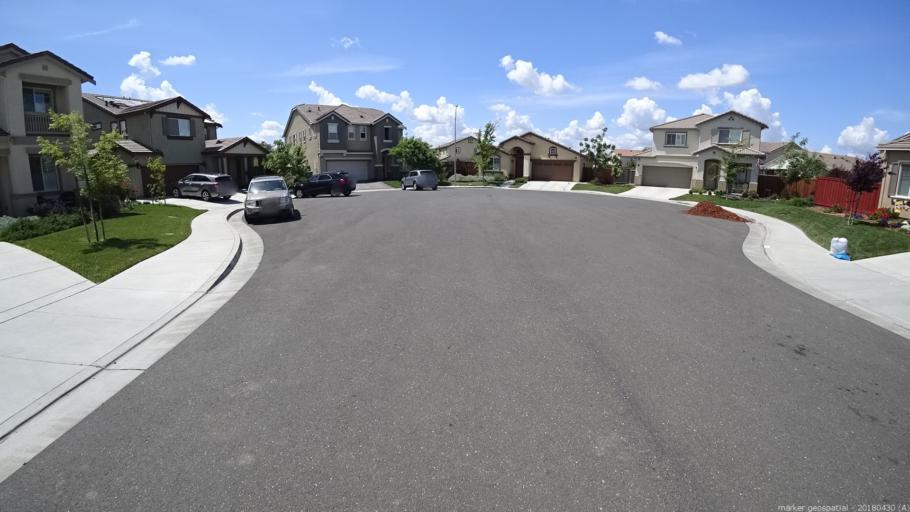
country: US
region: California
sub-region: Yolo County
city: West Sacramento
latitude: 38.5482
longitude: -121.5217
